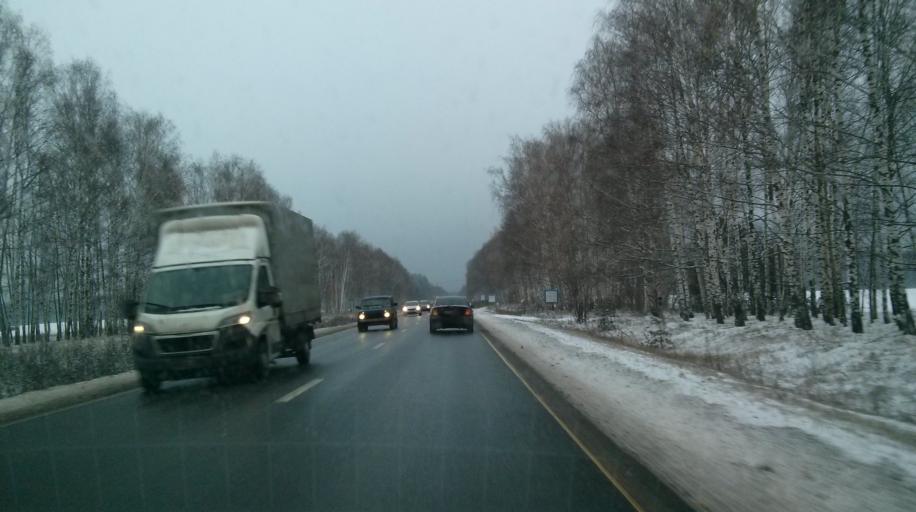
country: RU
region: Nizjnij Novgorod
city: Vorsma
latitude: 56.0298
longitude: 43.3612
